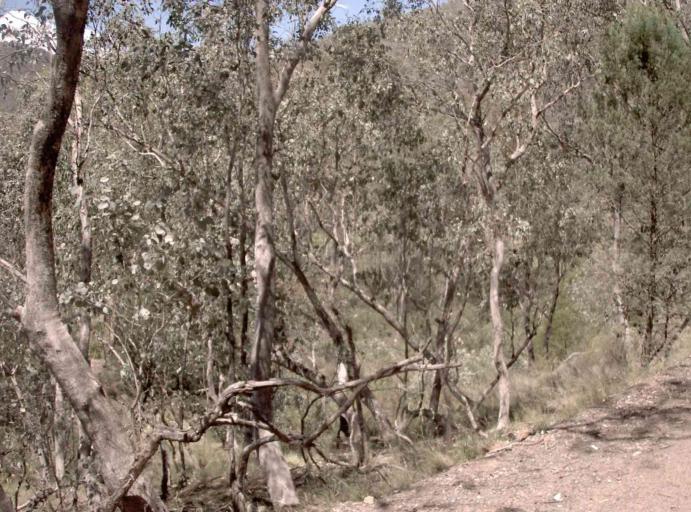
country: AU
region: New South Wales
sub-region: Snowy River
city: Jindabyne
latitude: -37.0786
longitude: 148.4870
